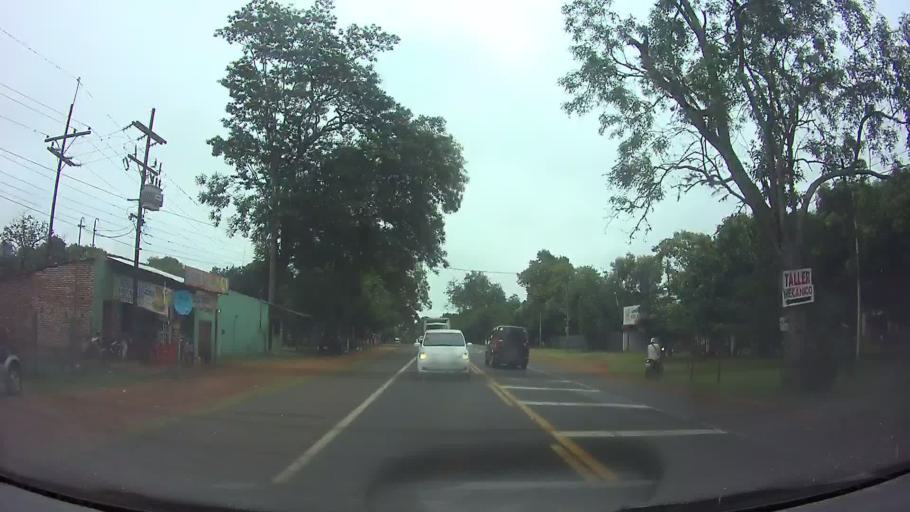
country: PY
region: Paraguari
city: Paraguari
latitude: -25.5985
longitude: -57.2038
